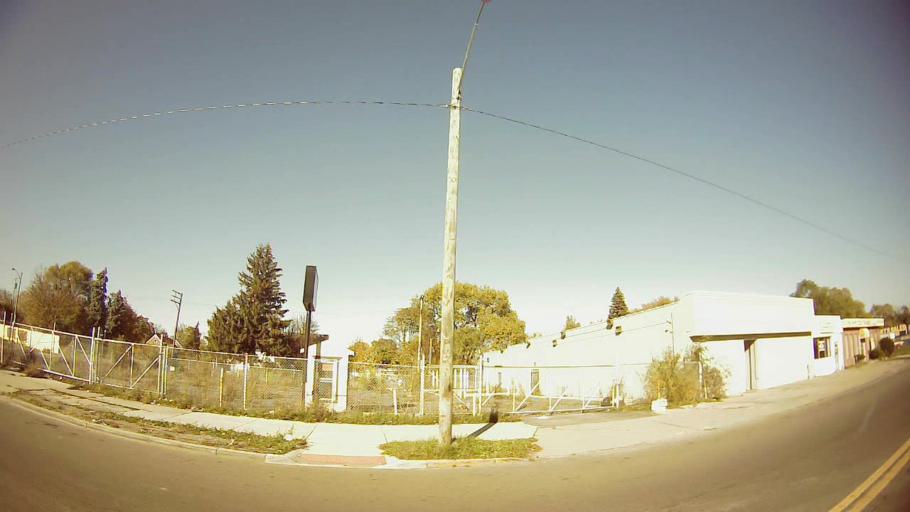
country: US
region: Michigan
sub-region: Wayne County
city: Highland Park
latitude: 42.4330
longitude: -83.0688
